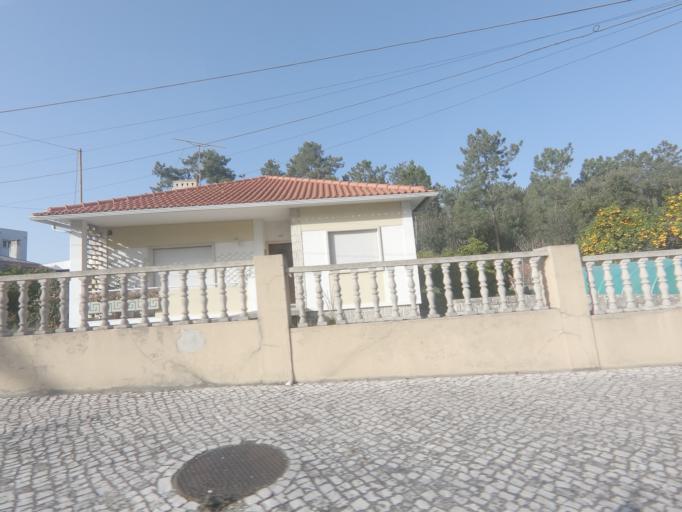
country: PT
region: Leiria
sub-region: Marinha Grande
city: Marinha Grande
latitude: 39.7479
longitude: -8.9116
